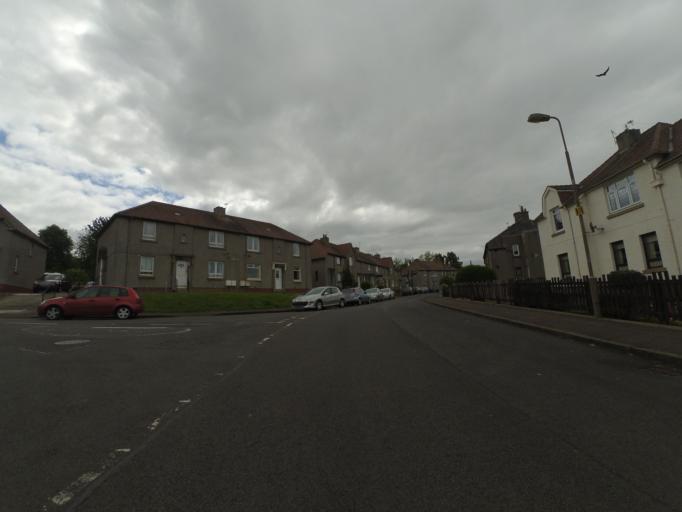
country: GB
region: Scotland
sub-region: West Lothian
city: Linlithgow
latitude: 55.9731
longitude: -3.6065
